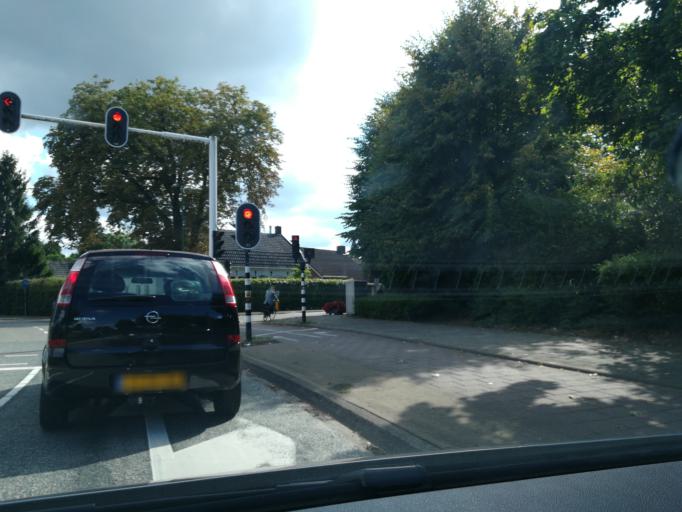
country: NL
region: North Brabant
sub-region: Gemeente Waalre
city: Waalre
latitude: 51.3896
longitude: 5.4444
